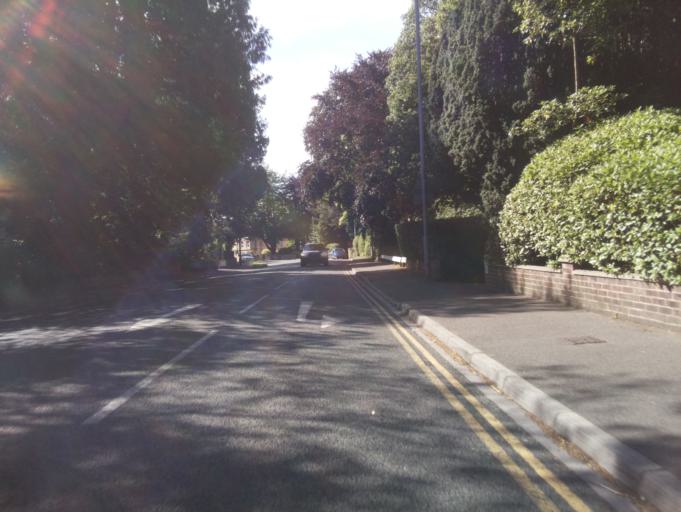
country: GB
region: England
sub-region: Bournemouth
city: Bournemouth
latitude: 50.7285
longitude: -1.9057
